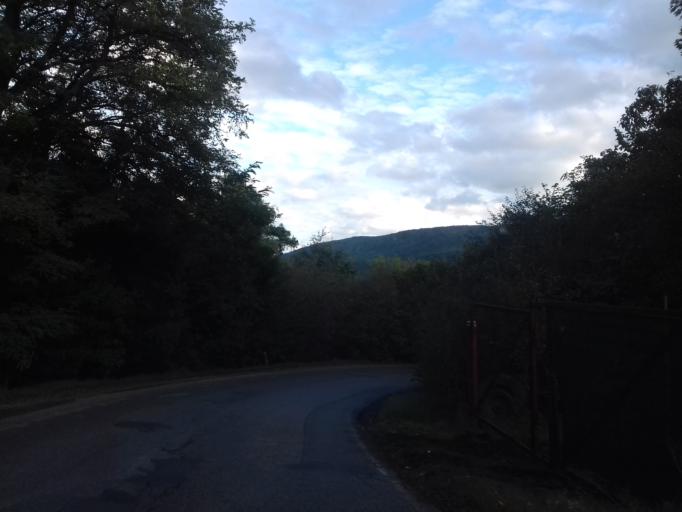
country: CZ
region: Central Bohemia
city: Revnice
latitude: 49.9248
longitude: 14.2461
